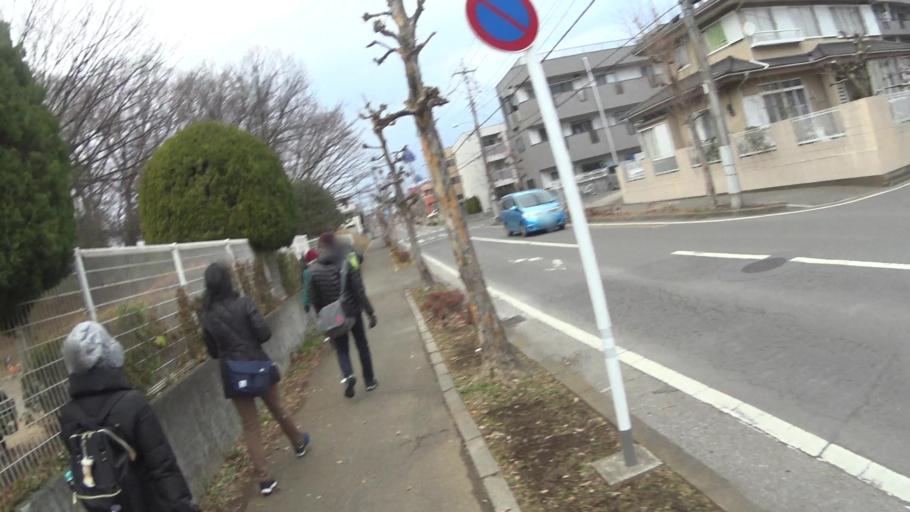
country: JP
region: Saitama
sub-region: Kawaguchi-shi
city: Hatogaya-honcho
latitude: 35.8656
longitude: 139.7023
